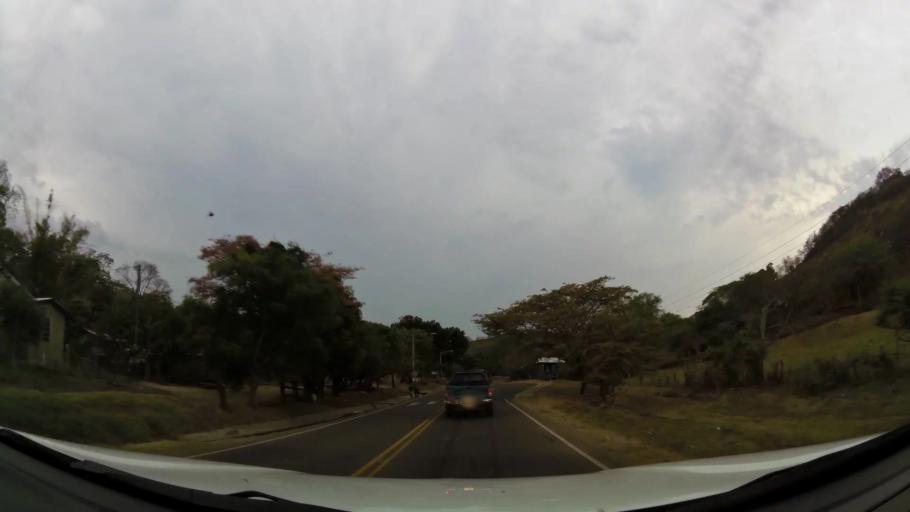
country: NI
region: Esteli
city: Esteli
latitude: 13.0020
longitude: -86.3066
